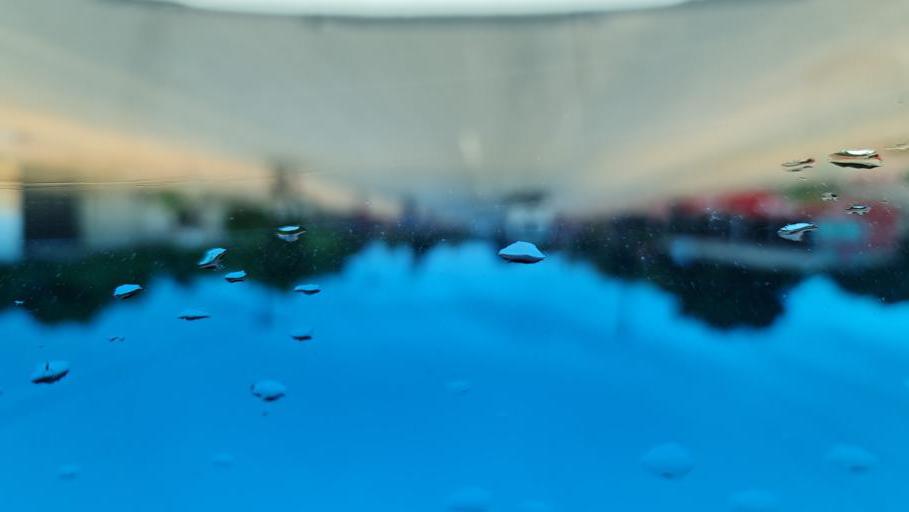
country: MZ
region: Nampula
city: Nampula
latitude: -15.1450
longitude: 39.2970
